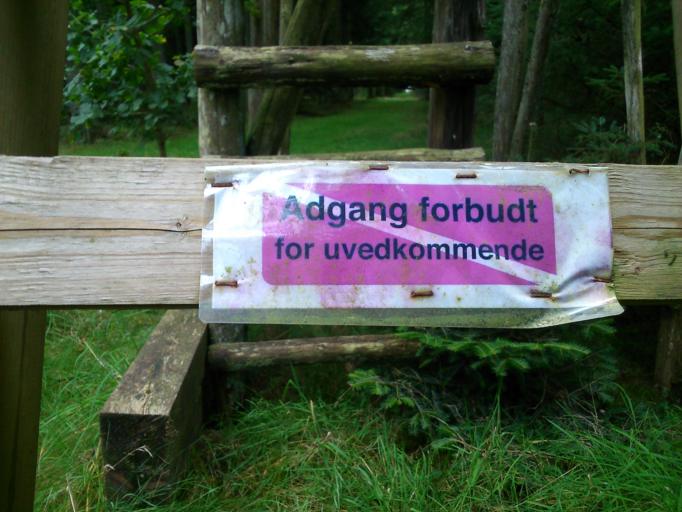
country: DK
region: Central Jutland
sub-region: Ringkobing-Skjern Kommune
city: Tarm
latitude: 55.8867
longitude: 8.4720
